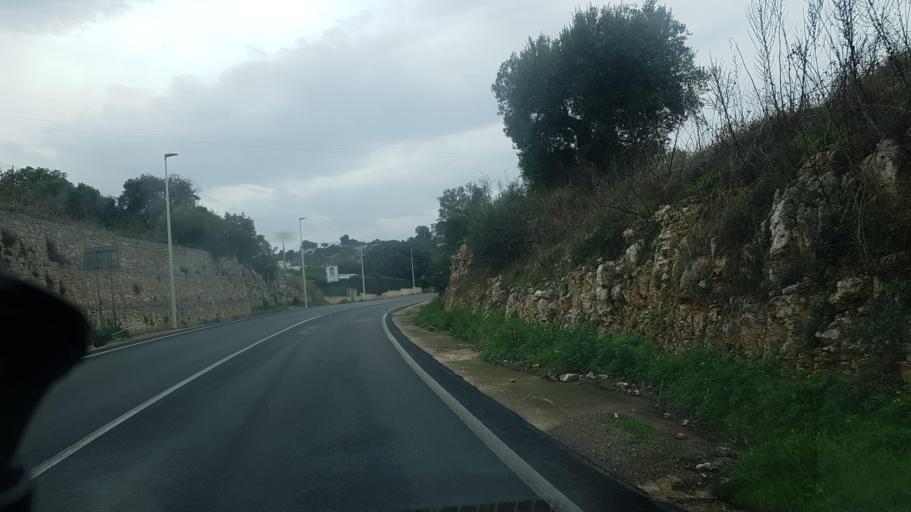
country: IT
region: Apulia
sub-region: Provincia di Brindisi
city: Ostuni
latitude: 40.7359
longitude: 17.5731
